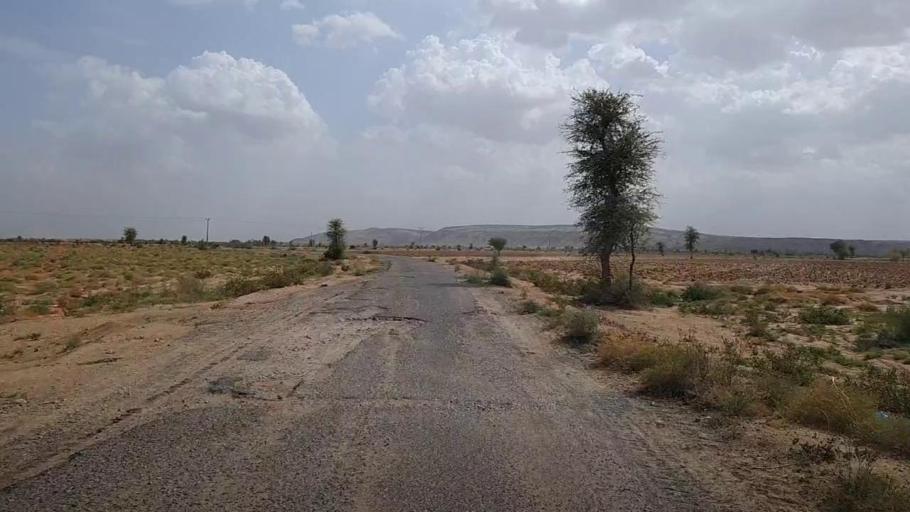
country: PK
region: Sindh
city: Jamshoro
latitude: 25.4010
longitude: 67.7669
